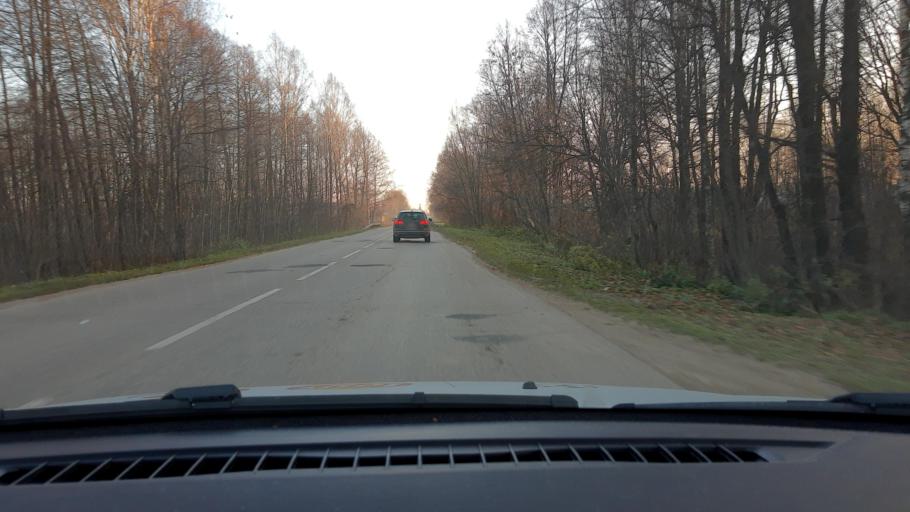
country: RU
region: Nizjnij Novgorod
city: Volodarsk
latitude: 56.2475
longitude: 43.1773
